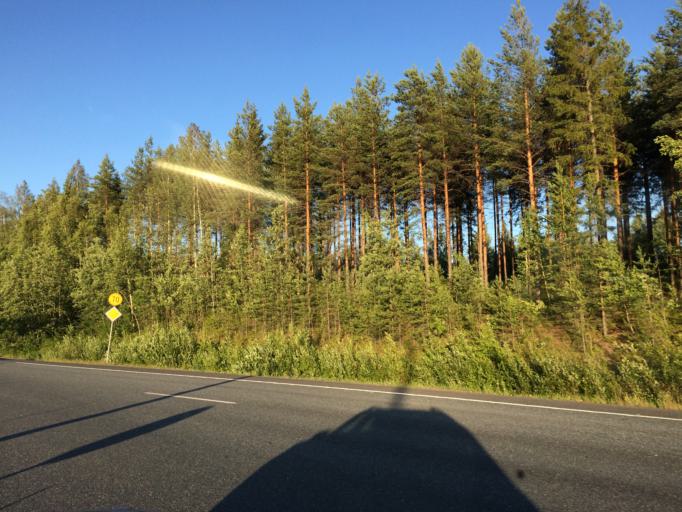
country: FI
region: Haeme
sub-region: Riihimaeki
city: Riihimaeki
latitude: 60.7493
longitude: 24.7221
